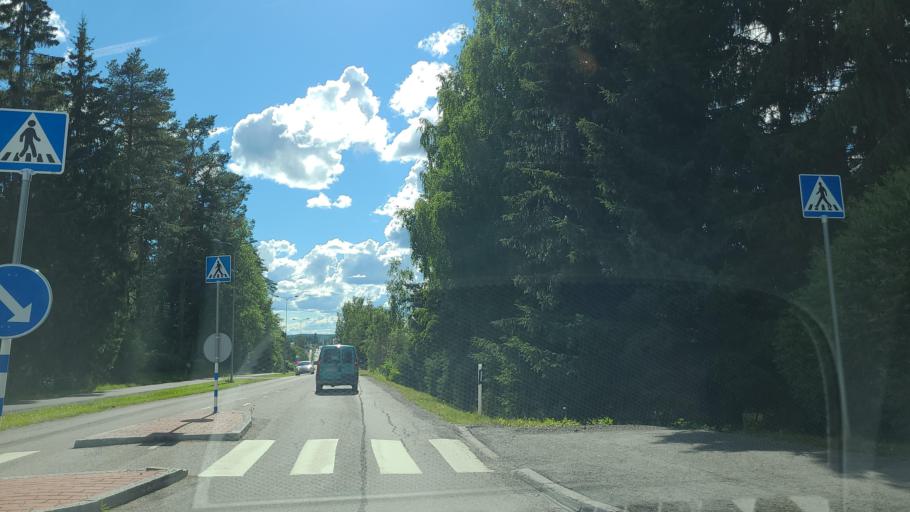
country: FI
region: Central Finland
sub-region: Jaemsae
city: Jaemsae
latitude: 61.8683
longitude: 25.2088
